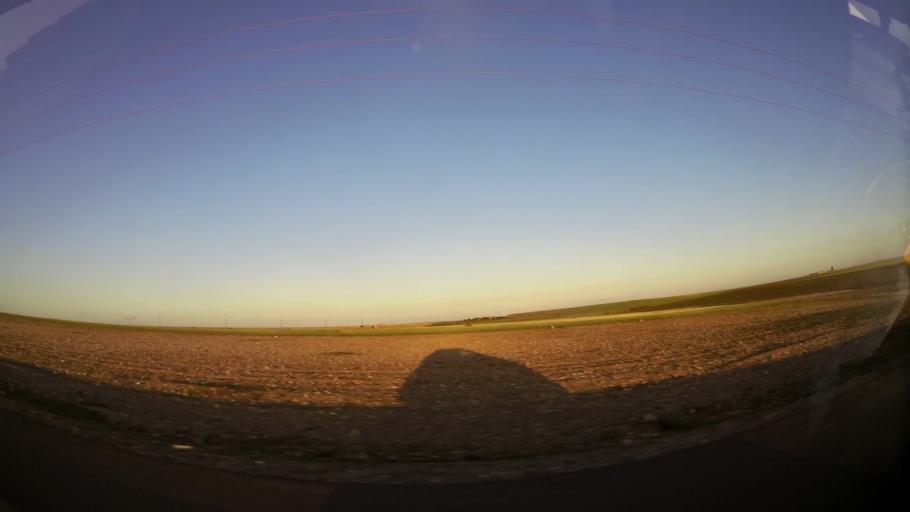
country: MA
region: Marrakech-Tensift-Al Haouz
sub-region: Kelaa-Des-Sraghna
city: Sidi Abdallah
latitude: 32.2361
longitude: -7.9286
